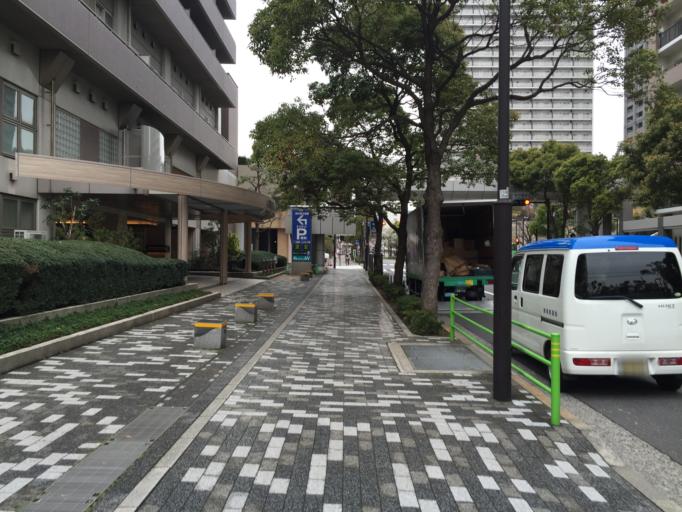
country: JP
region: Tokyo
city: Tokyo
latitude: 35.6575
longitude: 139.7842
